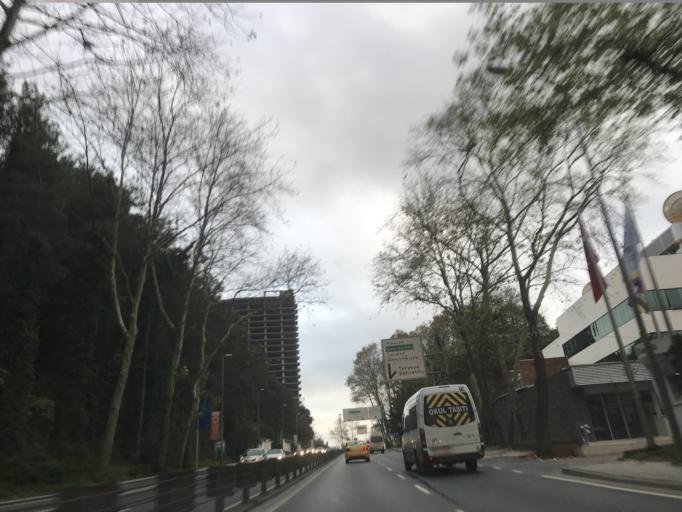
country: TR
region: Istanbul
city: Arikoey
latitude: 41.1439
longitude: 29.0283
